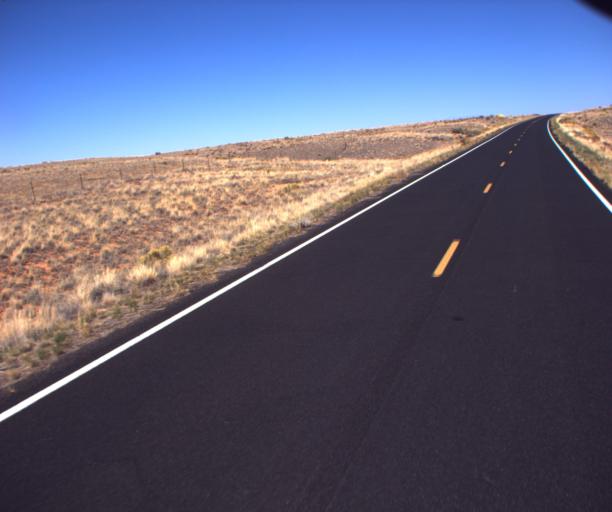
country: US
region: Arizona
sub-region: Navajo County
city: Dilkon
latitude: 35.2816
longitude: -110.4287
